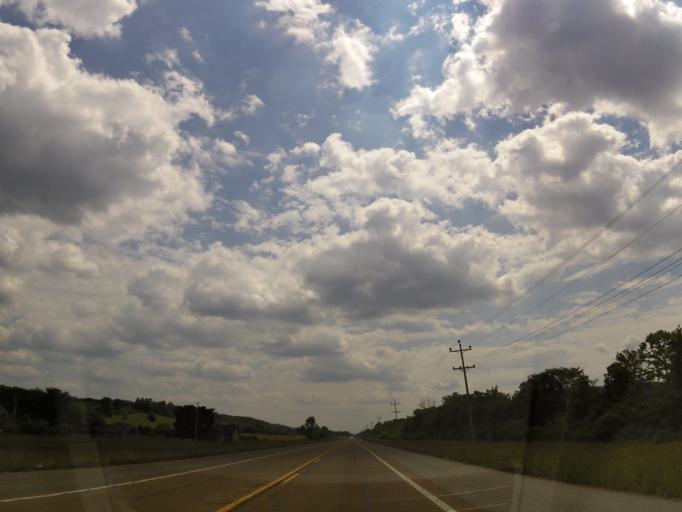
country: US
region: Tennessee
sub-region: Sequatchie County
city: Dunlap
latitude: 35.3361
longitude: -85.4161
